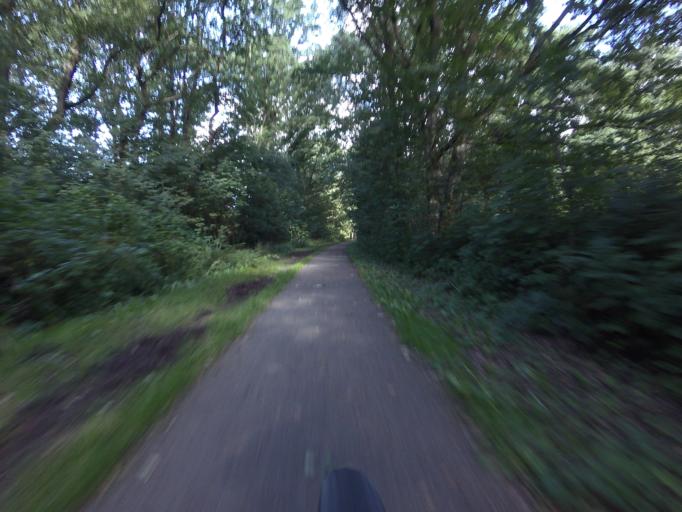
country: DK
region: Central Jutland
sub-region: Horsens Kommune
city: Braedstrup
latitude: 55.9685
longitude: 9.6934
